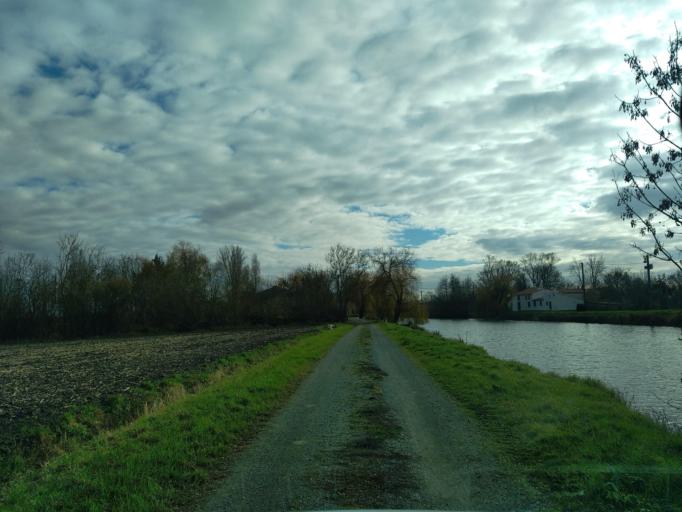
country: FR
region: Pays de la Loire
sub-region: Departement de la Vendee
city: Vix
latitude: 46.3269
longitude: -0.8044
